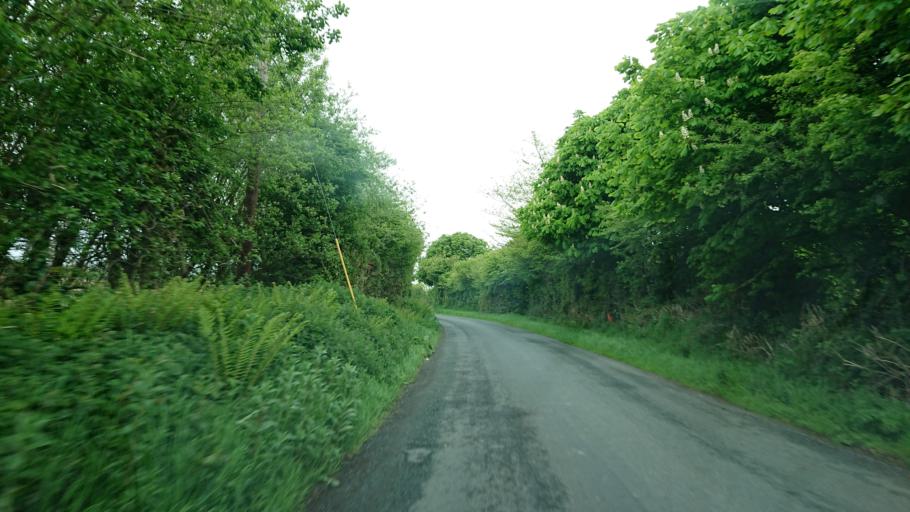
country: IE
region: Munster
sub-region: Waterford
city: Waterford
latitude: 52.2221
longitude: -7.0353
